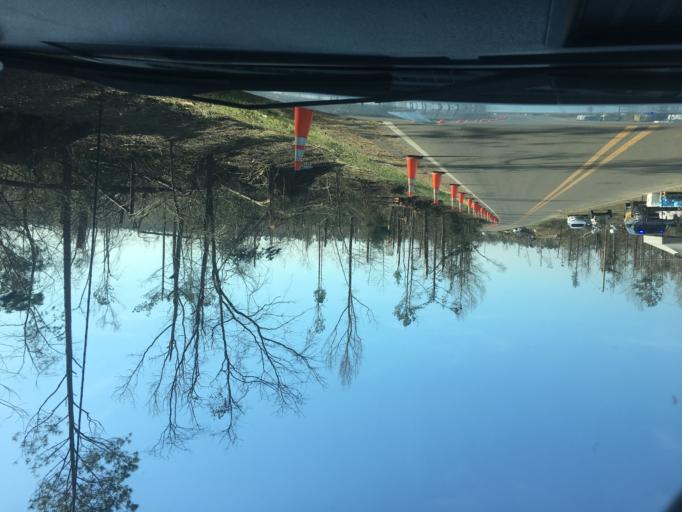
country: US
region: Alabama
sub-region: Lee County
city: Opelika
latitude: 32.4782
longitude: -85.3677
